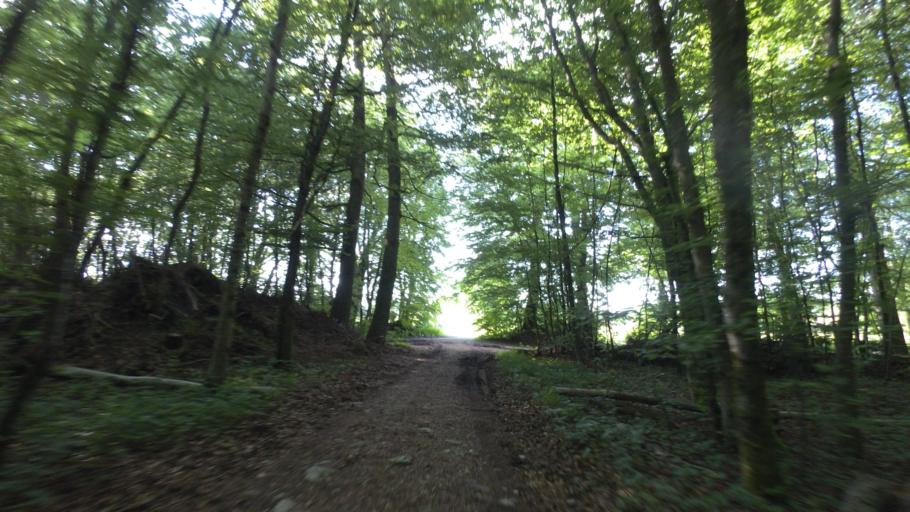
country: DE
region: Bavaria
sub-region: Upper Bavaria
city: Nussdorf
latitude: 47.8961
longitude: 12.5741
